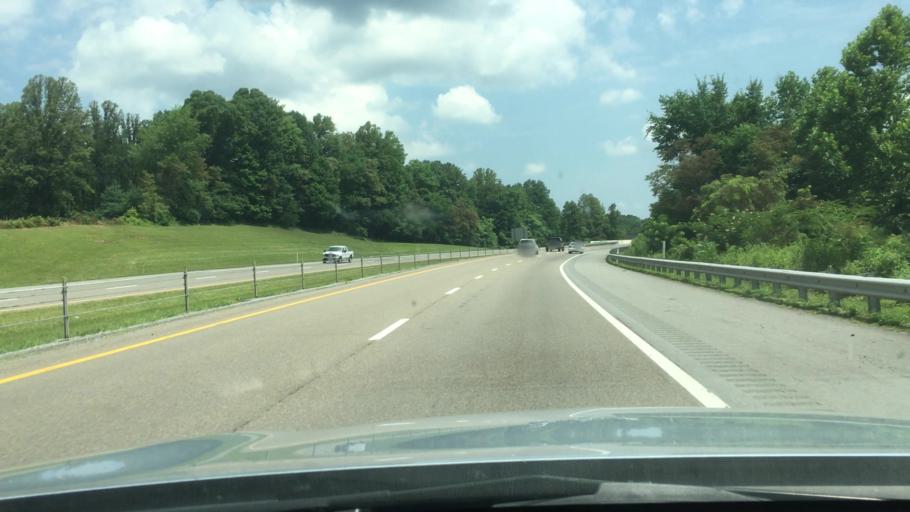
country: US
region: Tennessee
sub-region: Unicoi County
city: Unicoi
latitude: 36.2283
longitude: -82.3394
